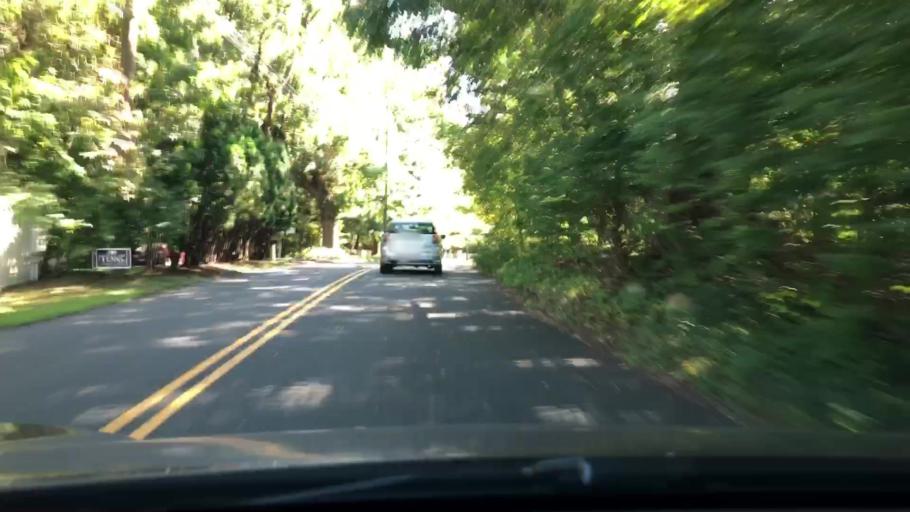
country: US
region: Connecticut
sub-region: Fairfield County
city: Darien
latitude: 41.1146
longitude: -73.4669
